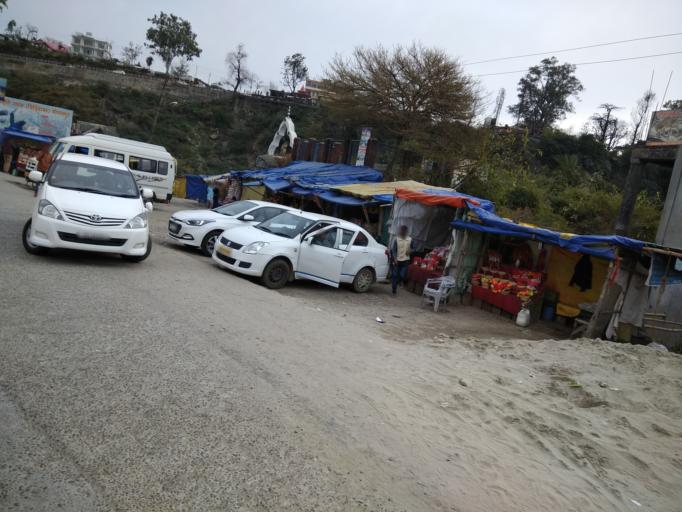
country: IN
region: Himachal Pradesh
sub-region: Kangra
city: Dharmsala
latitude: 32.1488
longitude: 76.4204
